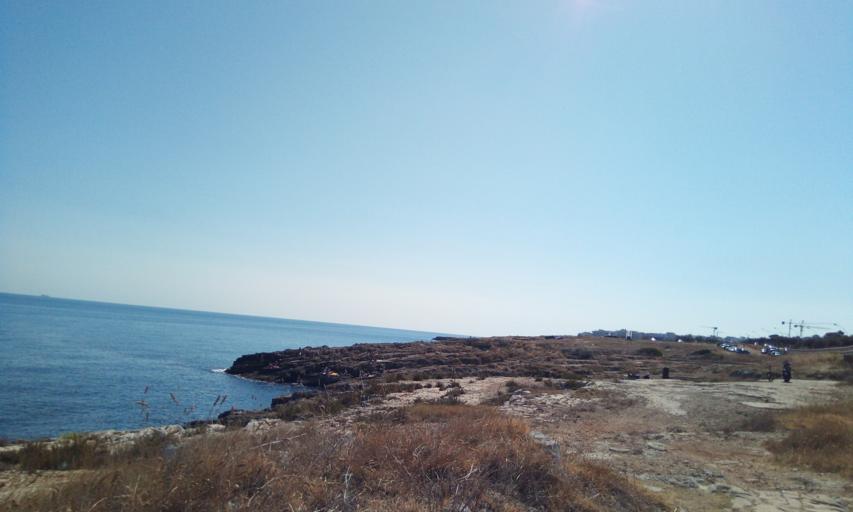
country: IT
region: Apulia
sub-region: Provincia di Bari
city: Polignano a Mare
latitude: 41.0015
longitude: 17.2053
